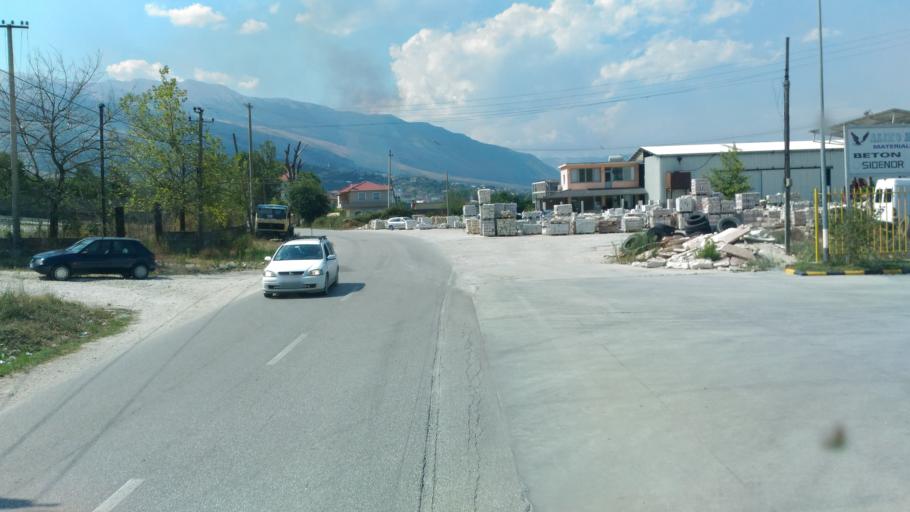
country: AL
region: Gjirokaster
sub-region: Rrethi i Gjirokastres
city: Lazarat
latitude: 40.0637
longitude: 20.1710
